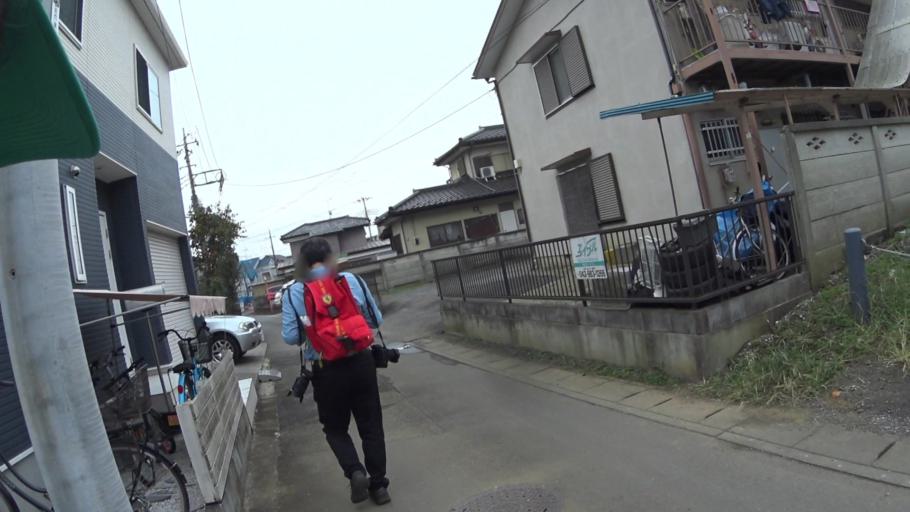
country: JP
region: Saitama
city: Hanno
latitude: 35.8599
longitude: 139.3197
